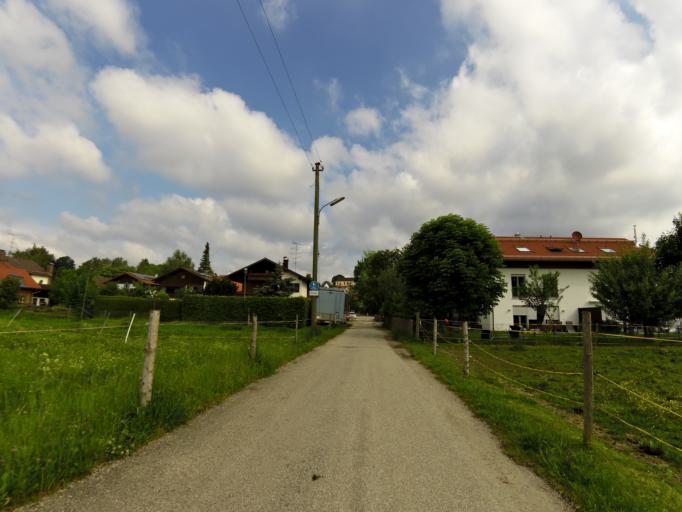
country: DE
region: Bavaria
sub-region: Upper Bavaria
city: Schaftlarn
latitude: 47.9888
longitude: 11.4542
